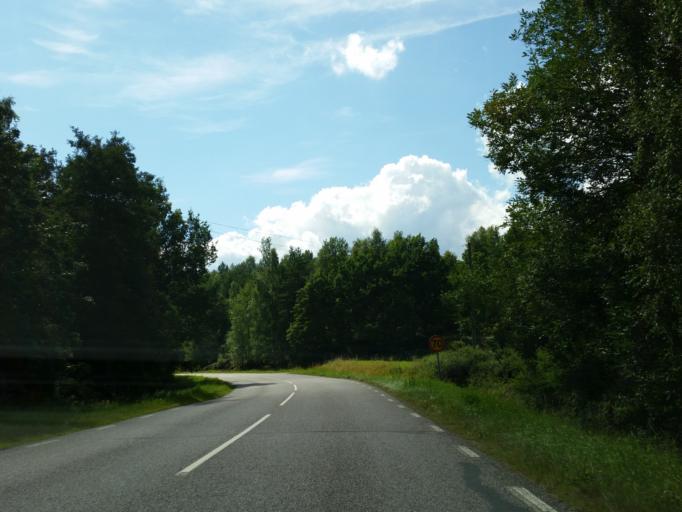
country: SE
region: Stockholm
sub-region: Sodertalje Kommun
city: Pershagen
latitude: 59.0082
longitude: 17.6598
